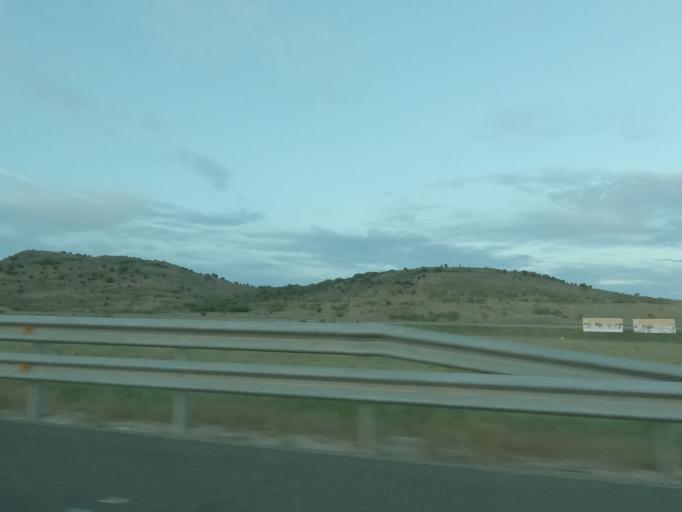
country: ES
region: Extremadura
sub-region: Provincia de Caceres
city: Caceres
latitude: 39.4234
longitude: -6.4021
